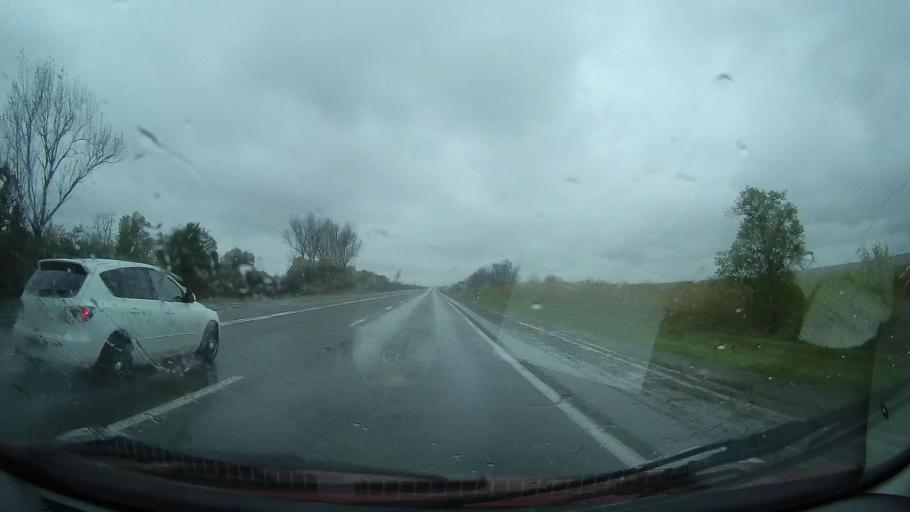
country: RU
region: Stavropol'skiy
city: Nevinnomyssk
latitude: 44.6309
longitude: 42.0265
